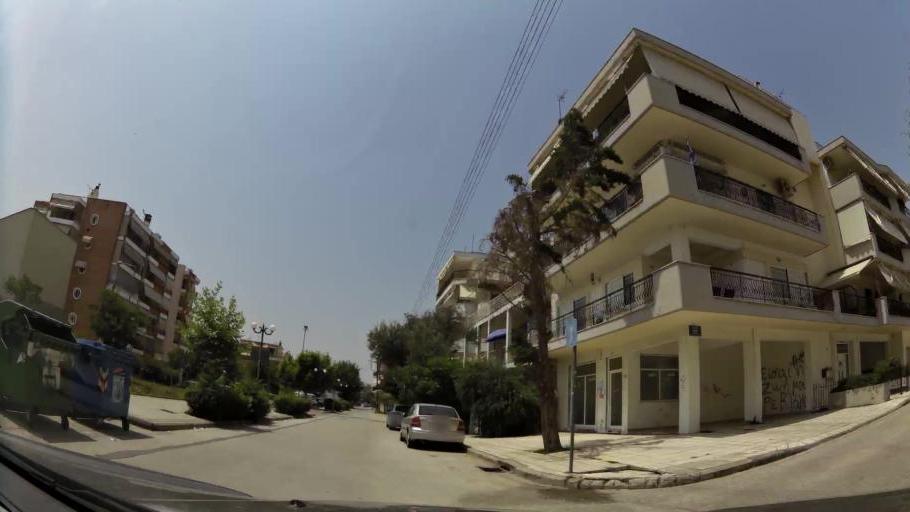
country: GR
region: Central Macedonia
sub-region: Nomos Thessalonikis
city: Evosmos
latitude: 40.6680
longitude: 22.9059
